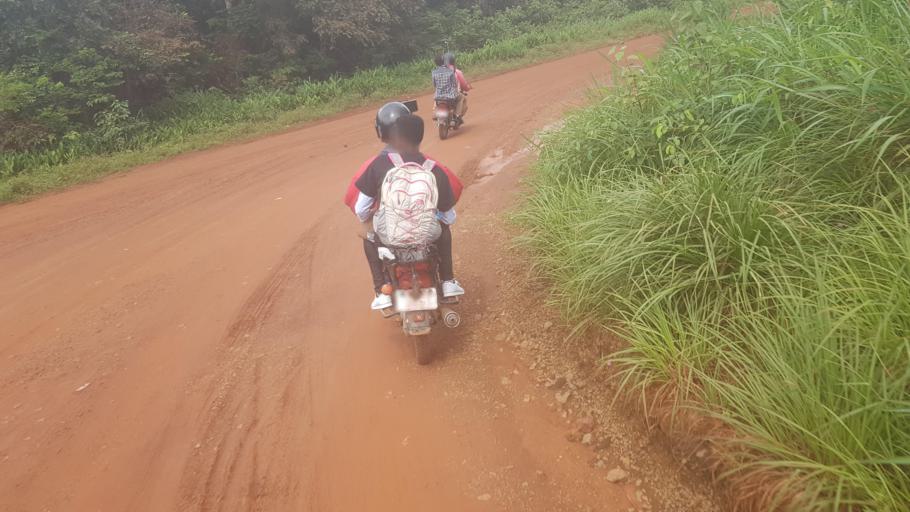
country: SL
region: Southern Province
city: Mogbwemo
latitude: 7.7658
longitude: -12.2994
